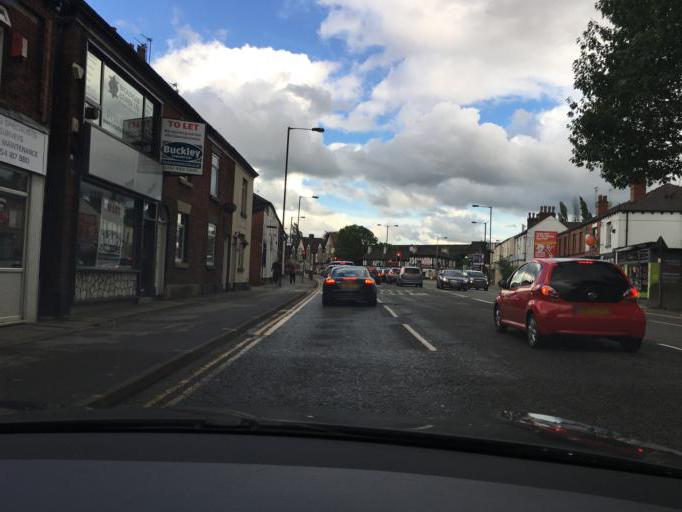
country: GB
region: England
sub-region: Borough of Stockport
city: Hazel Grove
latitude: 53.3762
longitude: -2.1147
